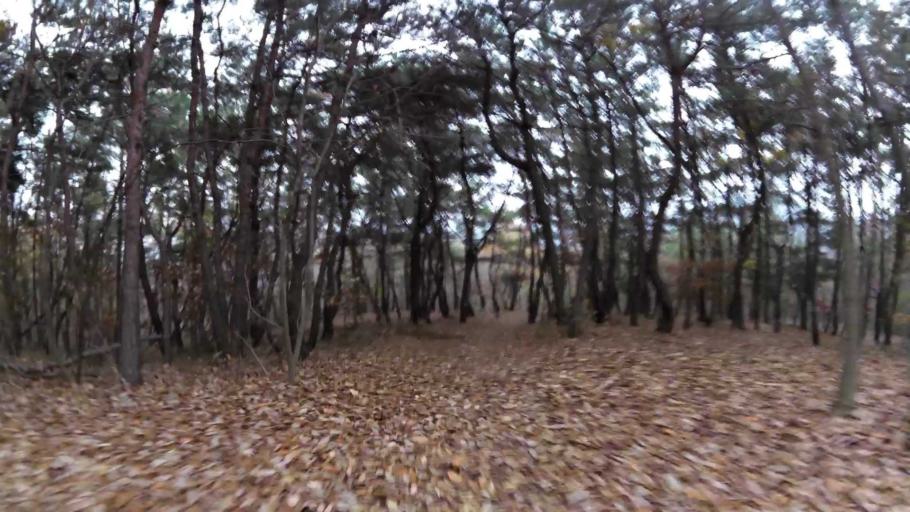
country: KR
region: Daegu
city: Daegu
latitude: 35.8622
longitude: 128.6680
